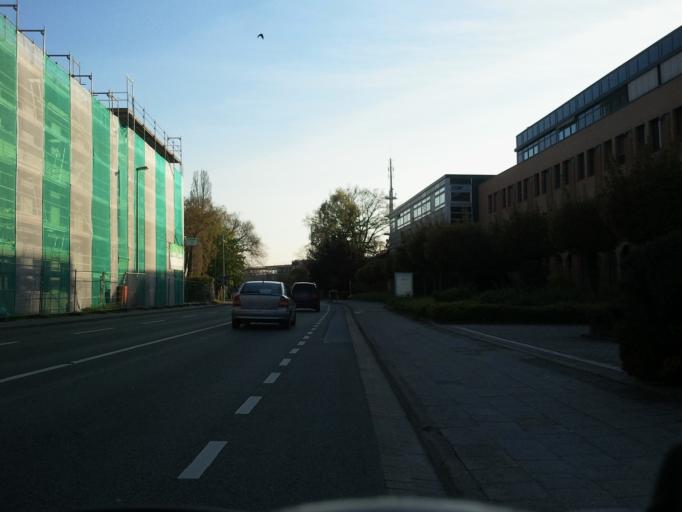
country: DE
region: Lower Saxony
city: Nienburg
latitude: 52.6463
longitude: 9.2116
